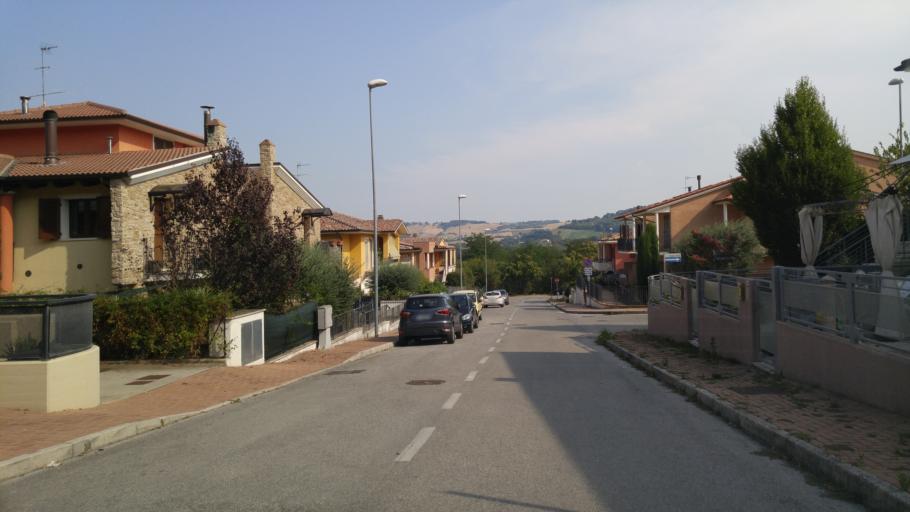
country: IT
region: The Marches
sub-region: Provincia di Pesaro e Urbino
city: Calcinelli
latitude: 43.7470
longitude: 12.9104
